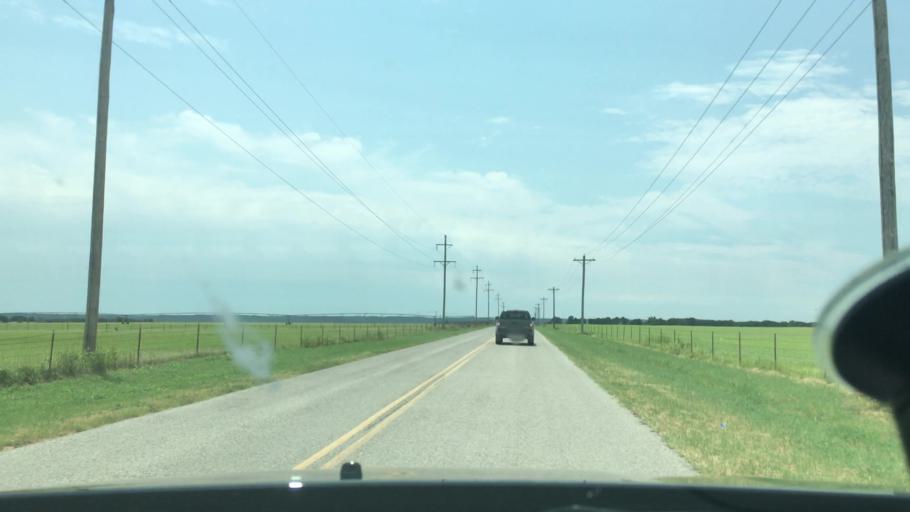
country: US
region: Oklahoma
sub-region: Love County
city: Marietta
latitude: 33.9212
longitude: -97.3521
